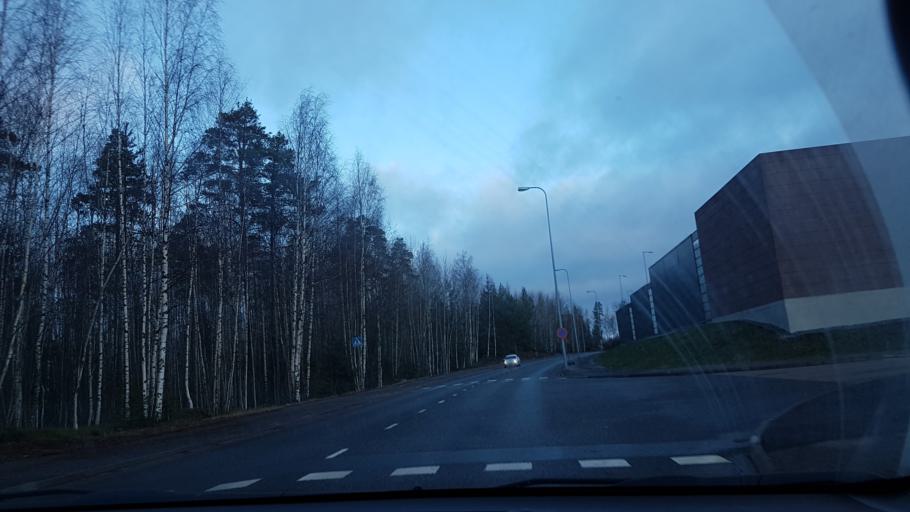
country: FI
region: Uusimaa
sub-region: Helsinki
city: Kilo
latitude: 60.3084
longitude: 24.8515
